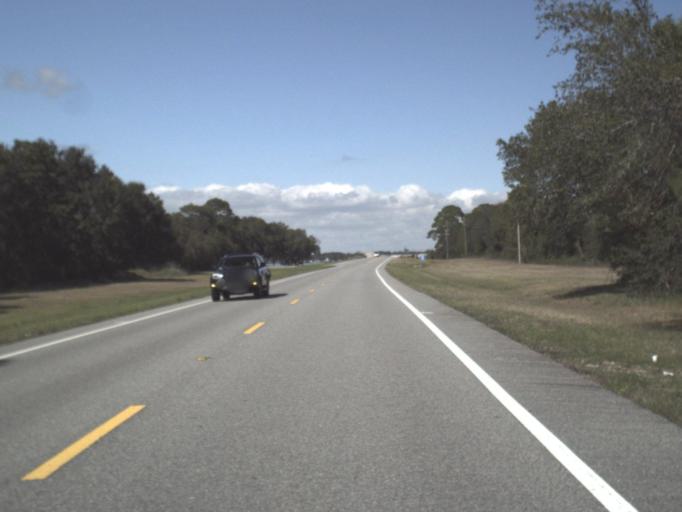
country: US
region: Florida
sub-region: Wakulla County
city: Crawfordville
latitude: 29.9577
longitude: -84.3850
